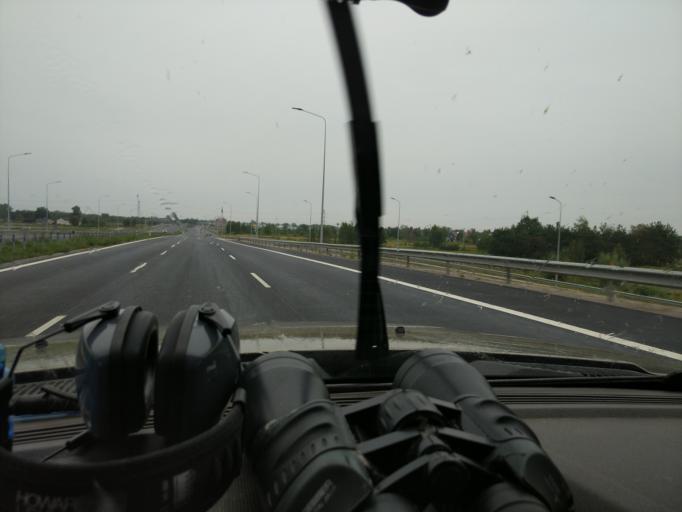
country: PL
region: Masovian Voivodeship
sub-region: Powiat wolominski
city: Radzymin
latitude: 52.3991
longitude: 21.2018
